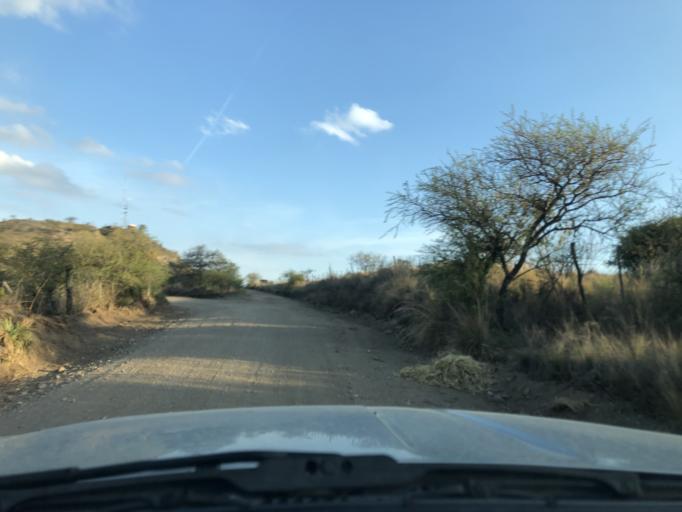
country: AR
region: Cordoba
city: Agua de Oro
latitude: -31.0626
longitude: -64.3477
